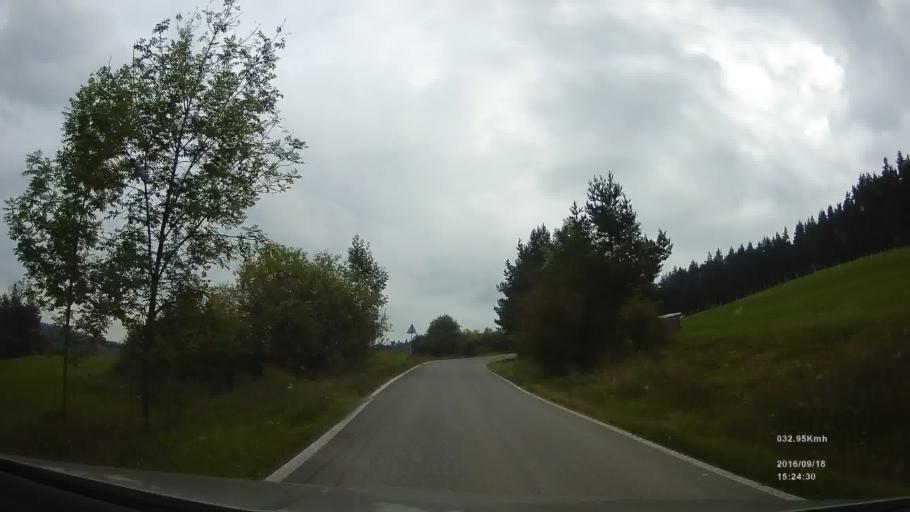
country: SK
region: Presovsky
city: Lubica
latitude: 49.0339
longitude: 20.4884
